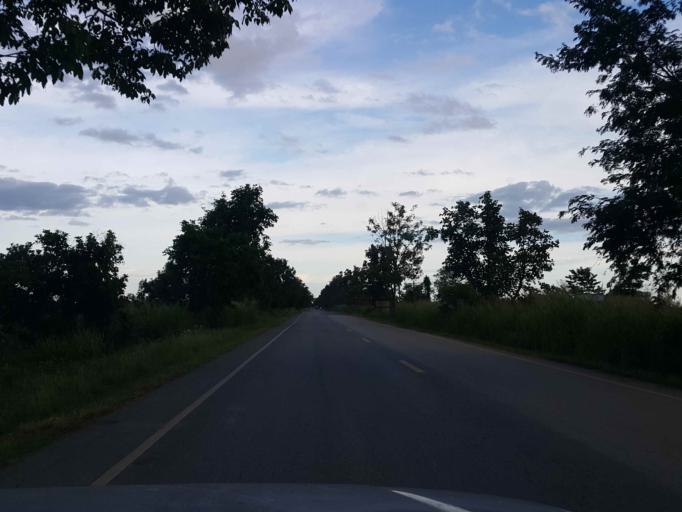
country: TH
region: Sukhothai
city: Sawankhalok
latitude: 17.3860
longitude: 99.7349
